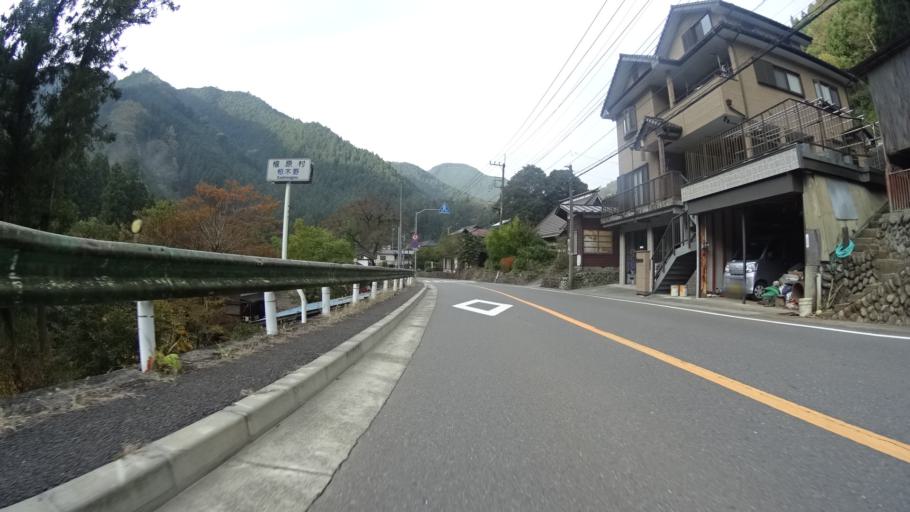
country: JP
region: Tokyo
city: Itsukaichi
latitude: 35.7028
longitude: 139.1413
